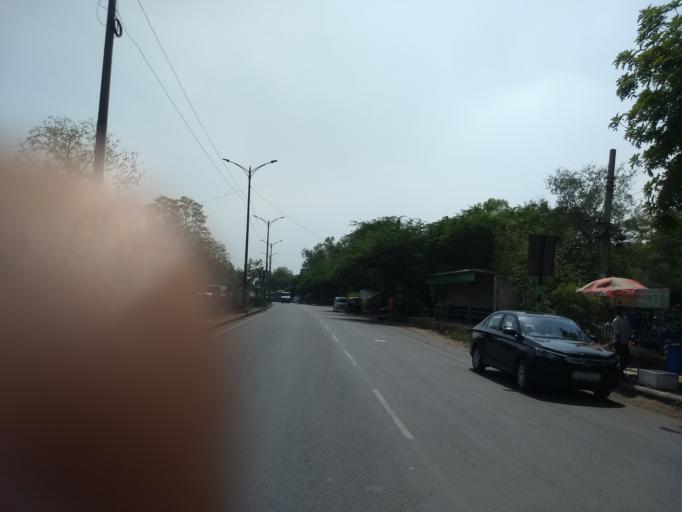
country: IN
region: Haryana
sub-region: Gurgaon
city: Gurgaon
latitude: 28.4699
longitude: 77.0464
